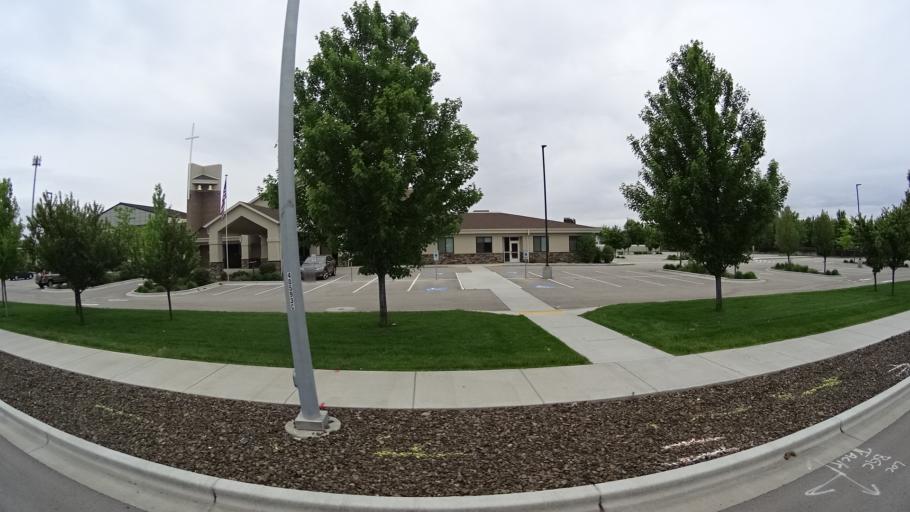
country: US
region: Idaho
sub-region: Ada County
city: Meridian
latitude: 43.6337
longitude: -116.3963
